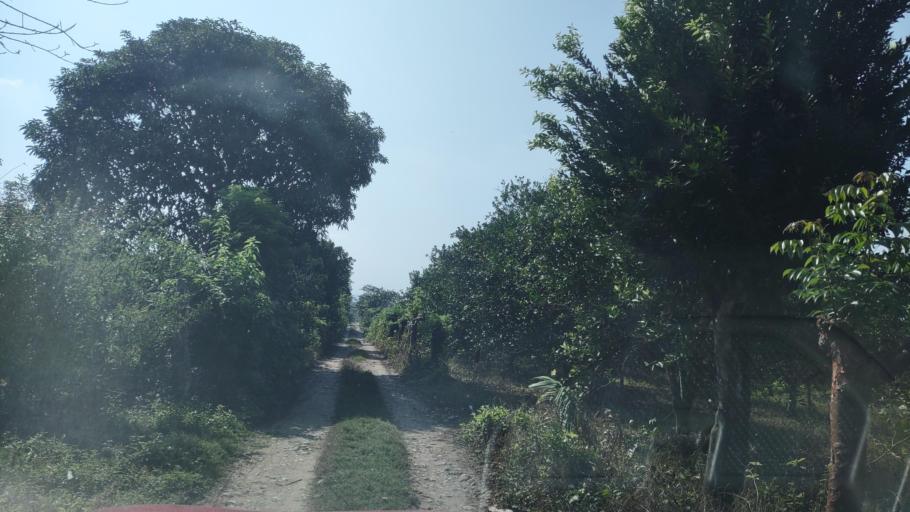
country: MX
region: Puebla
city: Espinal
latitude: 20.2400
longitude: -97.3460
